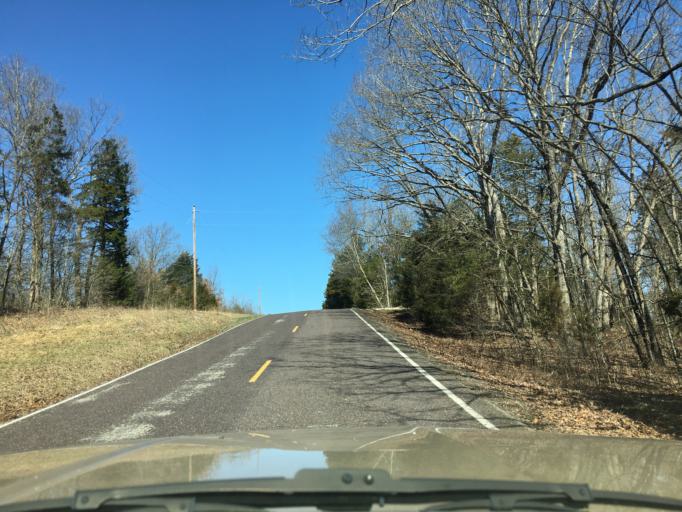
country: US
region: Missouri
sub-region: Franklin County
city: Gerald
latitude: 38.5183
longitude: -91.3264
